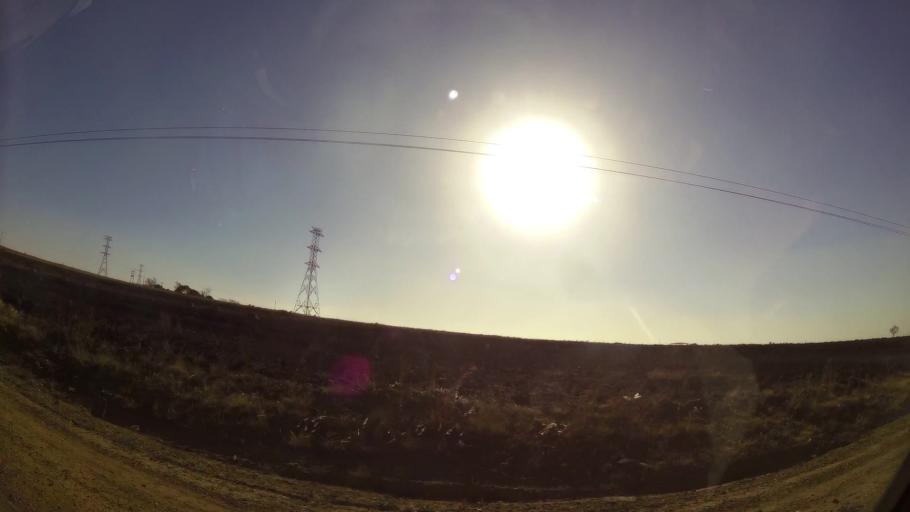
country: ZA
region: Gauteng
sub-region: City of Johannesburg Metropolitan Municipality
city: Diepsloot
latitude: -25.9645
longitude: 27.9540
